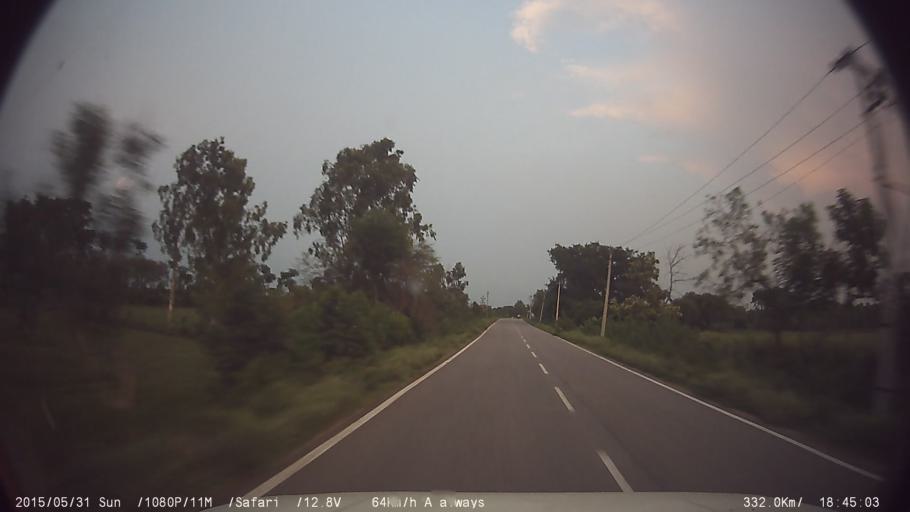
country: IN
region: Karnataka
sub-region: Mysore
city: Tirumakudal Narsipur
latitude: 12.1584
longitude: 76.8208
